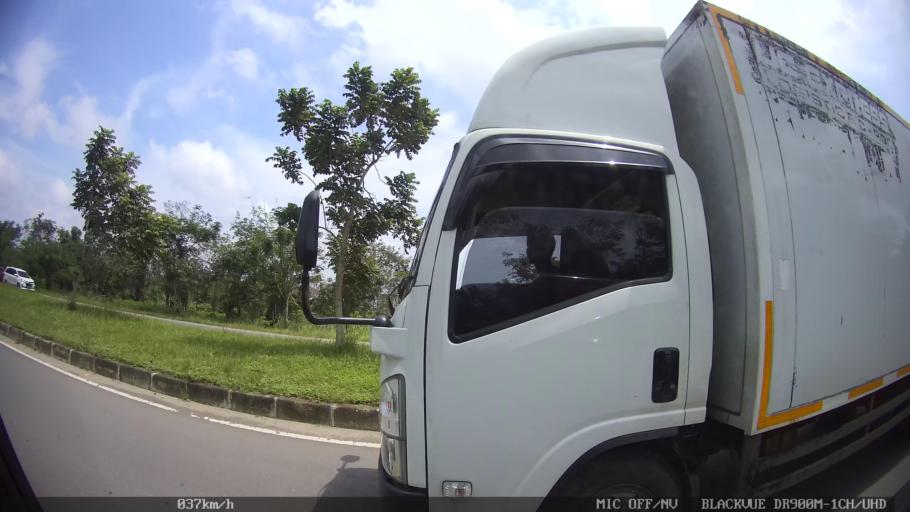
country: ID
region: Lampung
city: Kedaton
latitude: -5.3554
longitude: 105.3192
